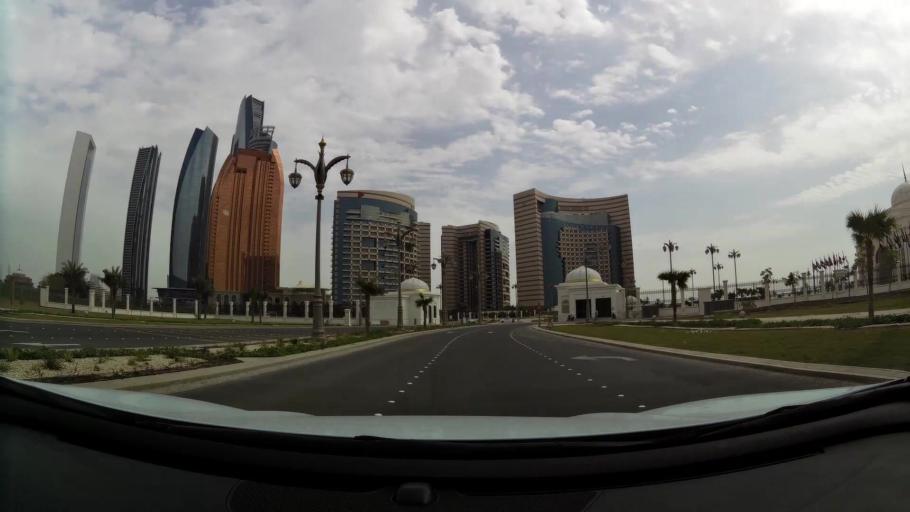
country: AE
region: Abu Dhabi
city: Abu Dhabi
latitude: 24.4574
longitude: 54.3158
